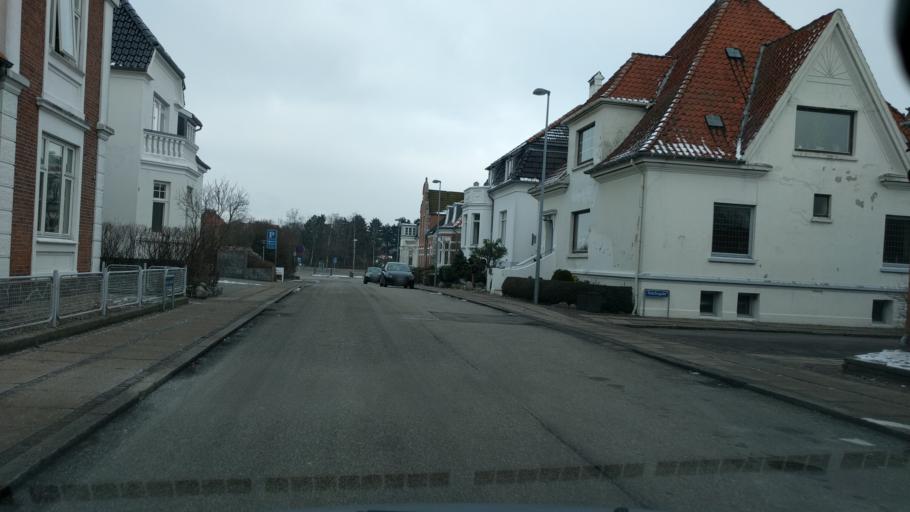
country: DK
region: Zealand
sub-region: Guldborgsund Kommune
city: Nykobing Falster
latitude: 54.7691
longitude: 11.8711
